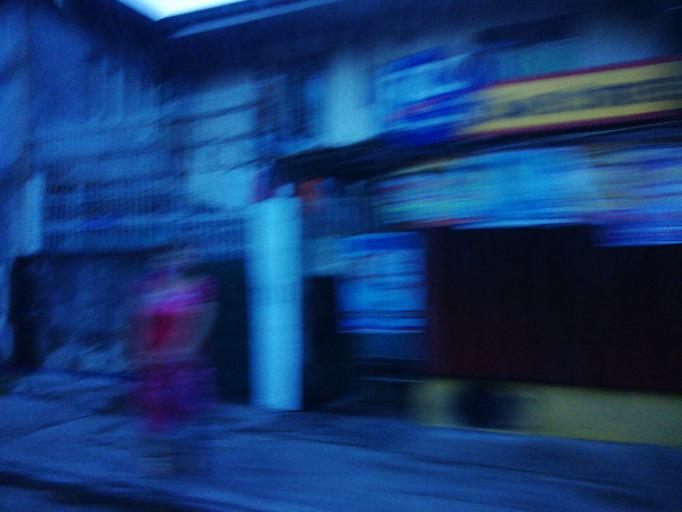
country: PH
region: Calabarzon
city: Bagong Pagasa
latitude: 14.6612
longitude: 121.0350
